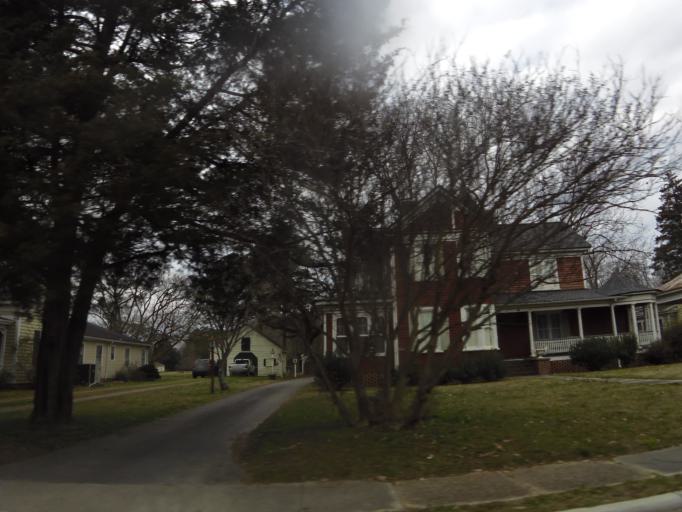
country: US
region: North Carolina
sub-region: Hertford County
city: Murfreesboro
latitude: 36.3307
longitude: -77.2140
